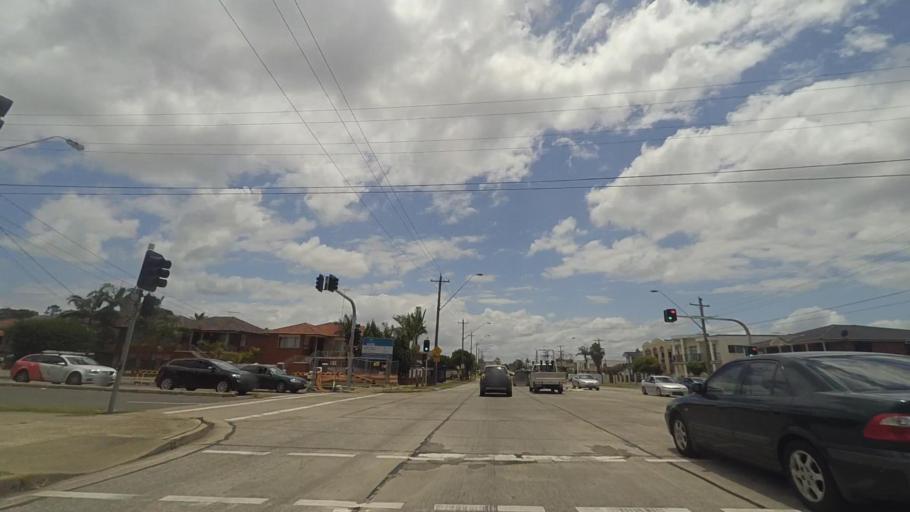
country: AU
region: New South Wales
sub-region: Fairfield
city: Cabramatta West
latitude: -33.8933
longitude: 150.9223
